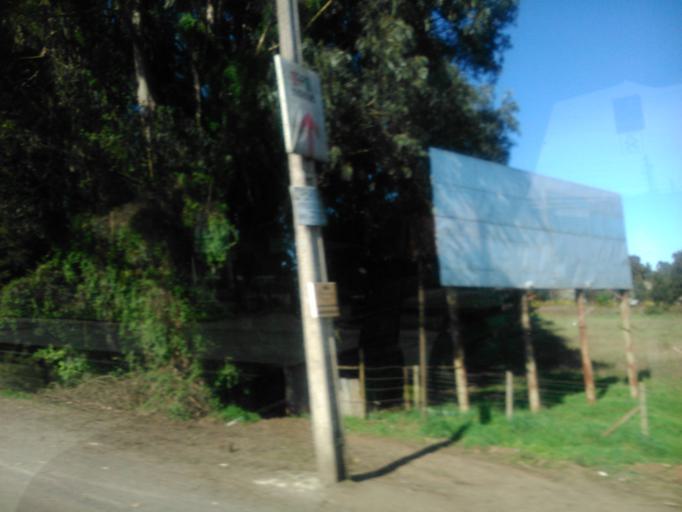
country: CL
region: Araucania
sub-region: Provincia de Cautin
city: Temuco
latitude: -38.7802
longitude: -72.6102
